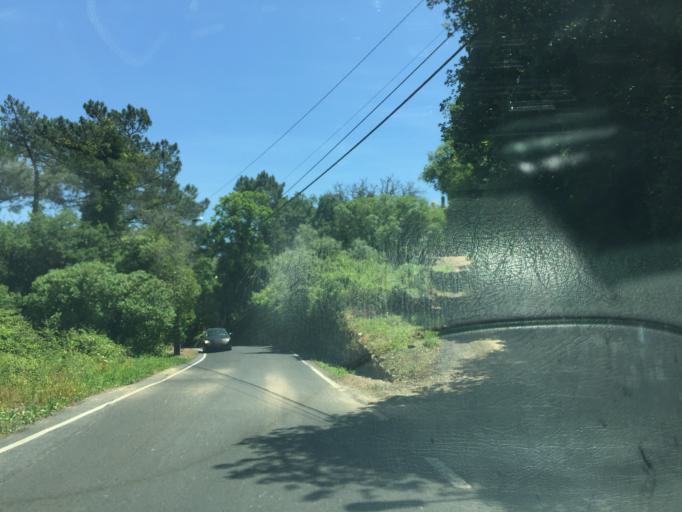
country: PT
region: Lisbon
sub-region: Mafra
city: Venda do Pinheiro
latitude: 38.8892
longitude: -9.2106
